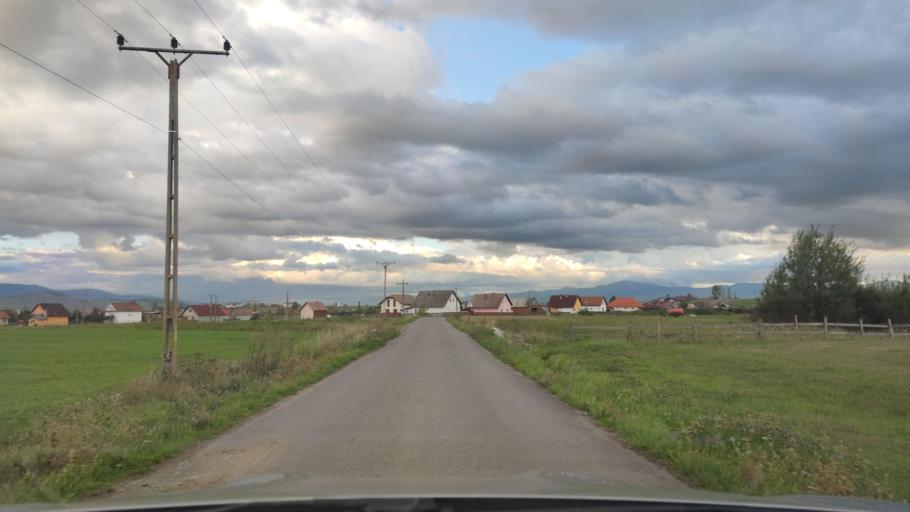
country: RO
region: Harghita
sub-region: Comuna Remetea
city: Remetea
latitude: 46.8070
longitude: 25.4391
